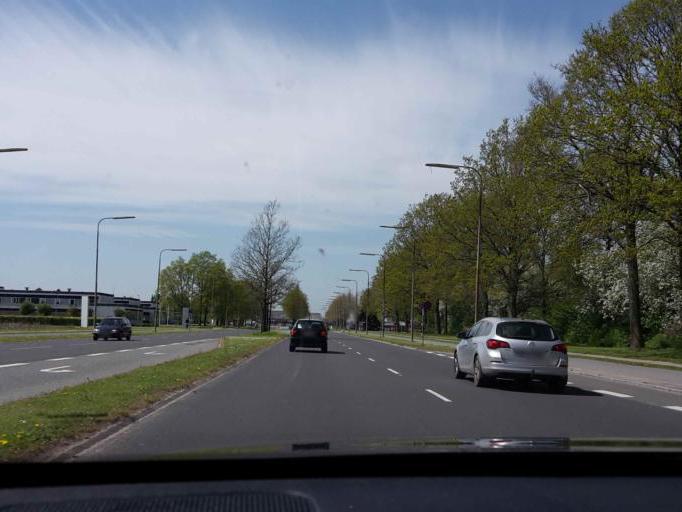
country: DK
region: South Denmark
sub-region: Odense Kommune
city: Odense
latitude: 55.3743
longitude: 10.4030
